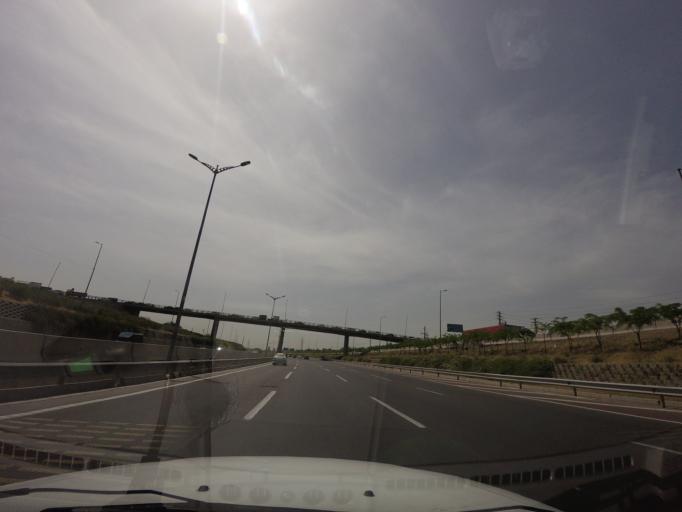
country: IR
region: Tehran
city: Eslamshahr
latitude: 35.6786
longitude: 51.2312
